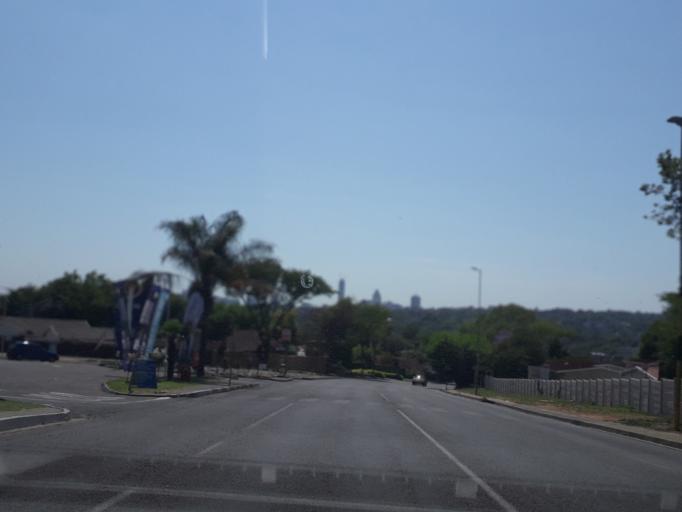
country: ZA
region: Gauteng
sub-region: City of Johannesburg Metropolitan Municipality
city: Johannesburg
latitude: -26.1140
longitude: 28.0144
